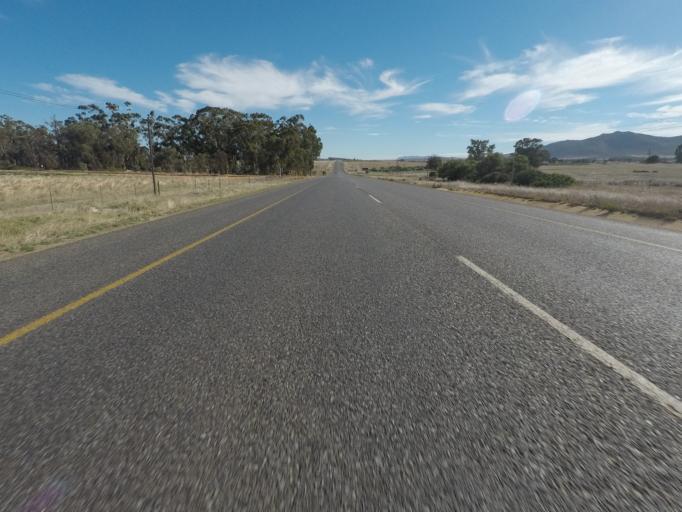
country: ZA
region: Western Cape
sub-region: West Coast District Municipality
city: Malmesbury
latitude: -33.6169
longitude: 18.7267
